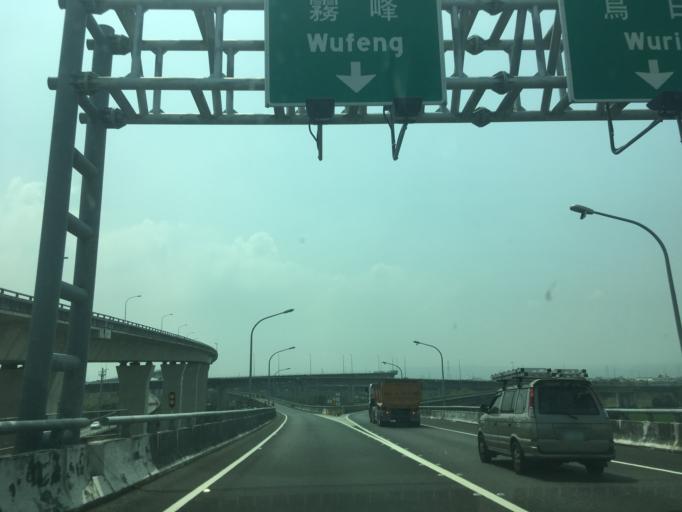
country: TW
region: Taiwan
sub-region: Taichung City
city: Taichung
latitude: 24.0541
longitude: 120.6829
